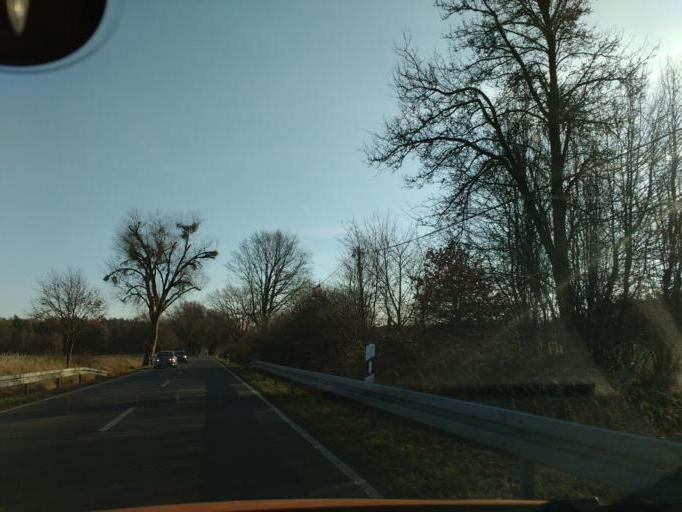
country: DE
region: Brandenburg
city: Protzel
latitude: 52.6425
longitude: 13.9696
